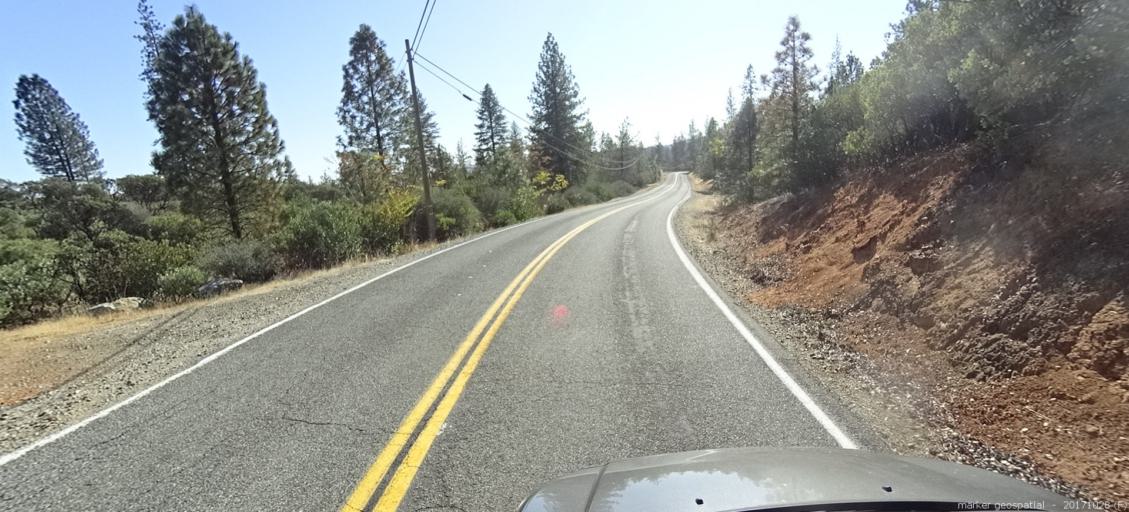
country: US
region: California
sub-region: Shasta County
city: Shasta
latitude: 40.6397
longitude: -122.4559
